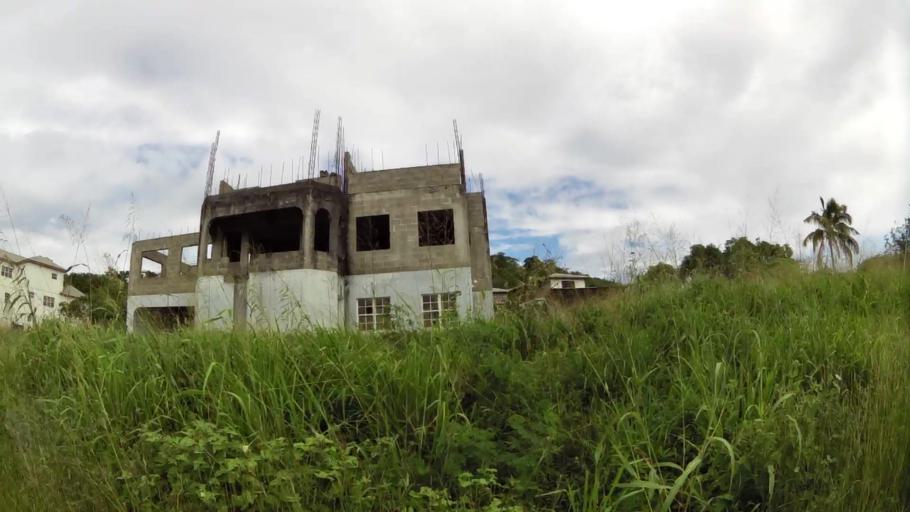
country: AG
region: Saint John
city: Potters Village
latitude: 17.0875
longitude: -61.8111
